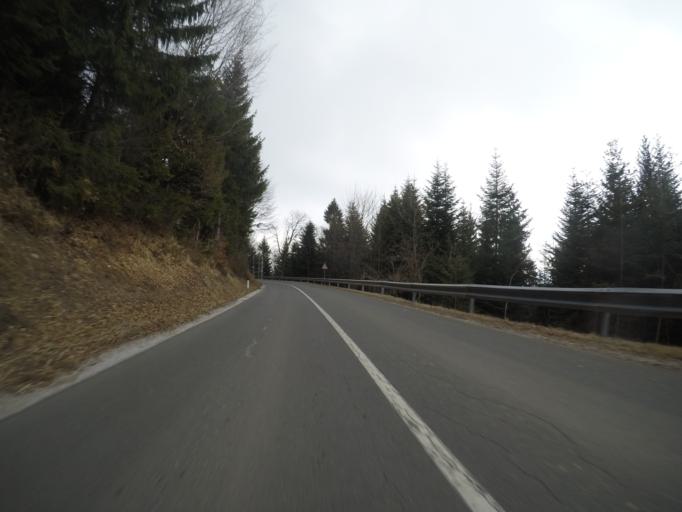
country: SI
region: Ruse
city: Ruse
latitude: 46.4913
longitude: 15.5280
